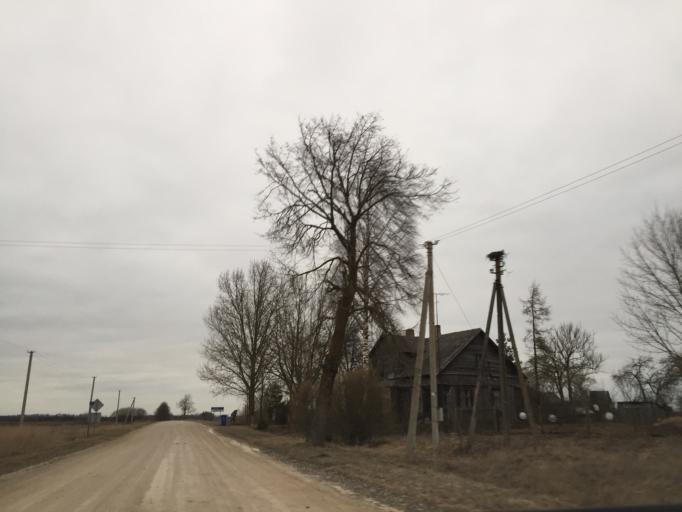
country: LT
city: Zagare
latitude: 56.2723
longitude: 23.2627
